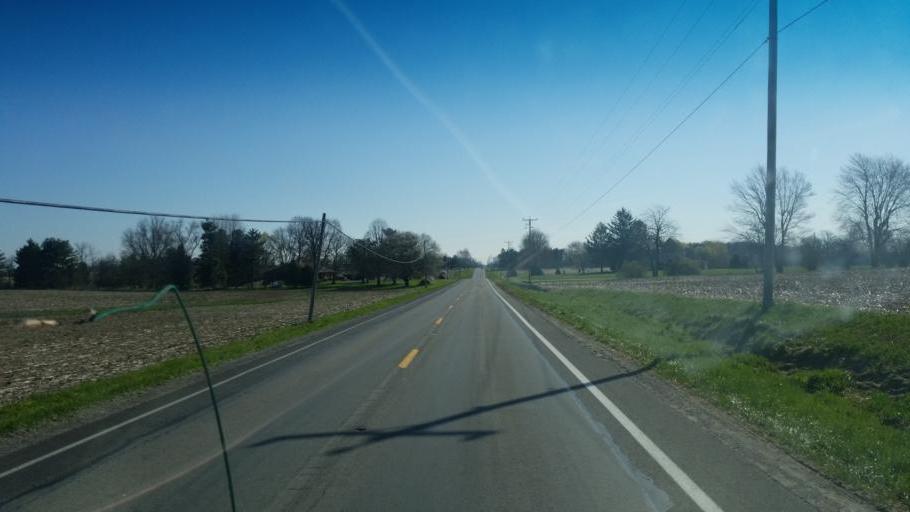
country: US
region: Ohio
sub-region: Hardin County
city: Kenton
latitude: 40.6604
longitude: -83.5681
